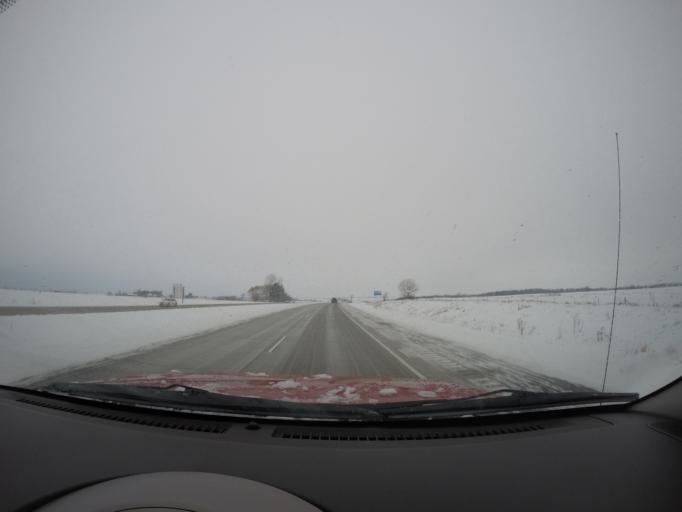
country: US
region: Minnesota
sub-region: Winona County
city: Saint Charles
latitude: 43.9524
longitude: -92.0693
